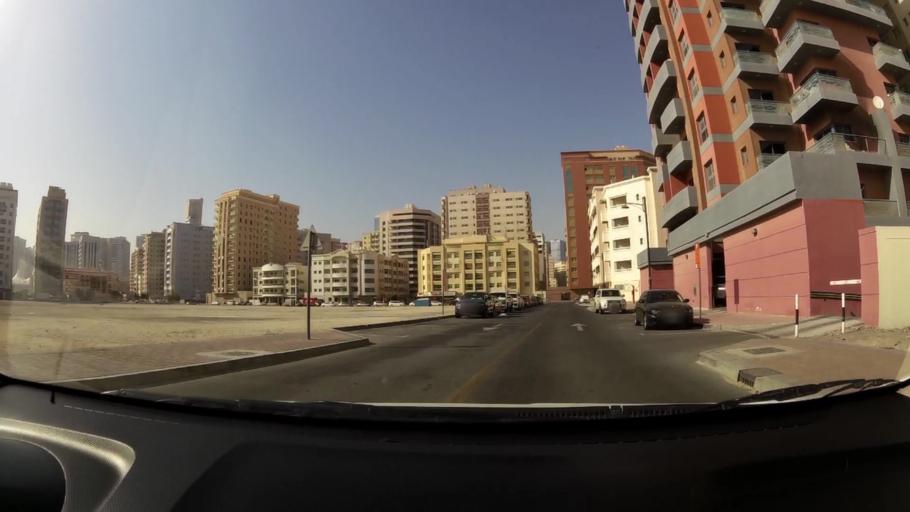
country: AE
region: Ash Shariqah
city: Sharjah
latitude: 25.2925
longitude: 55.3780
